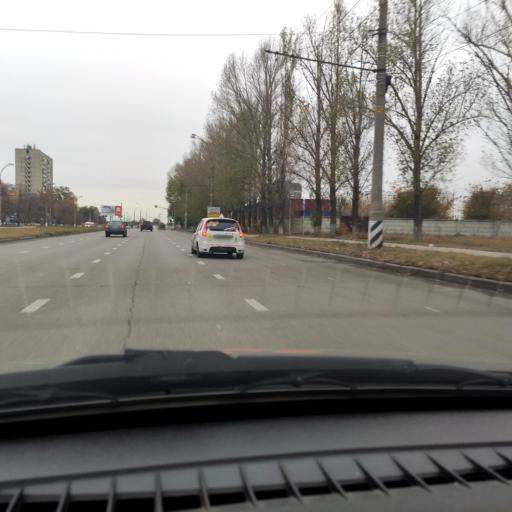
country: RU
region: Samara
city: Tol'yatti
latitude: 53.5132
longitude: 49.2571
